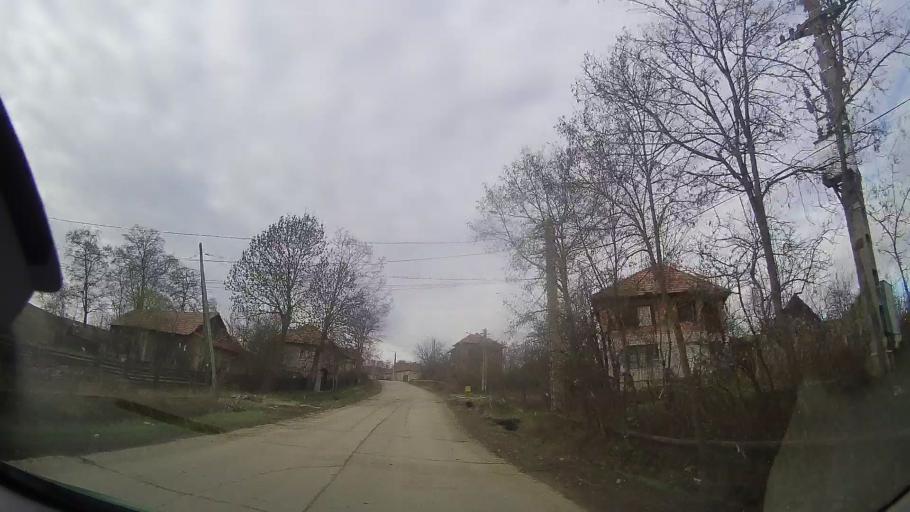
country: RO
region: Bistrita-Nasaud
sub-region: Comuna Sanmihaiu de Campie
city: Sanmihaiu de Campie
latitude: 46.8899
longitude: 24.3343
